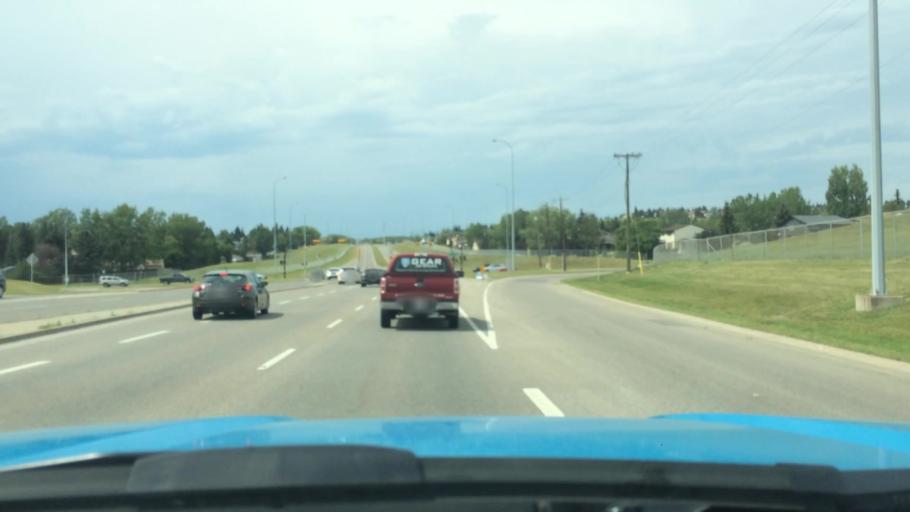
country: CA
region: Alberta
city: Calgary
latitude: 51.1145
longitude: -114.1527
